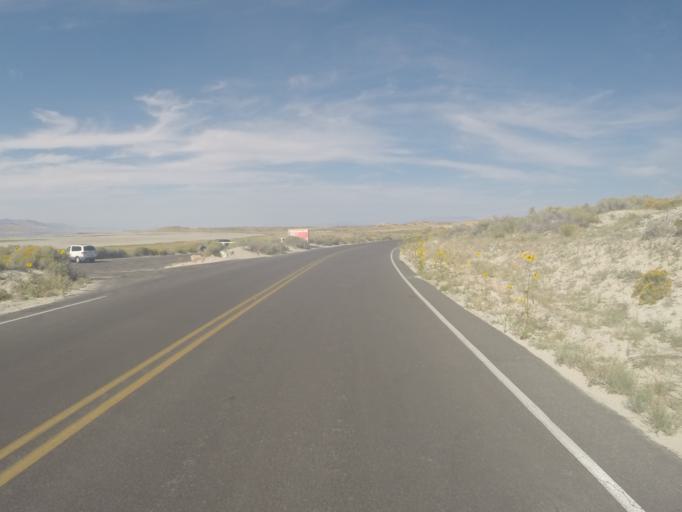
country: US
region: Utah
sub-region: Weber County
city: Hooper
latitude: 41.0476
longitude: -112.2502
